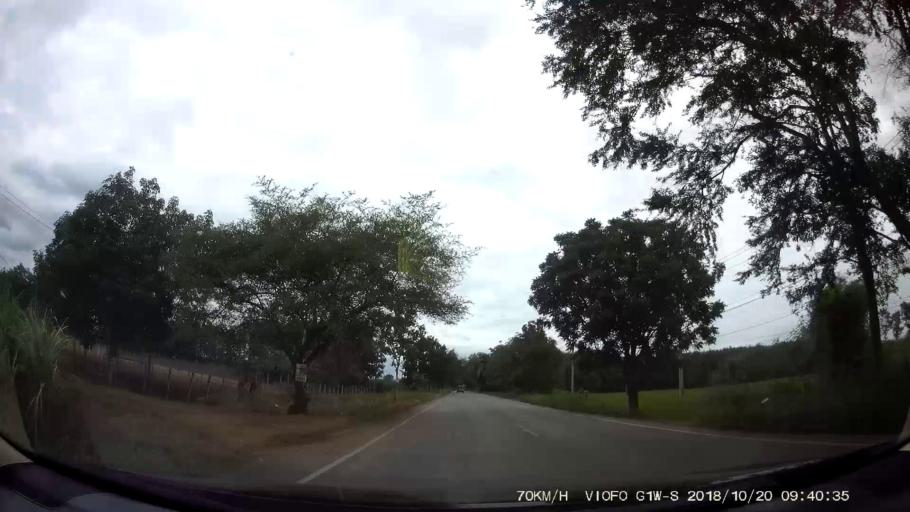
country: TH
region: Chaiyaphum
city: Kaset Sombun
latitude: 16.4444
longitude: 101.9609
